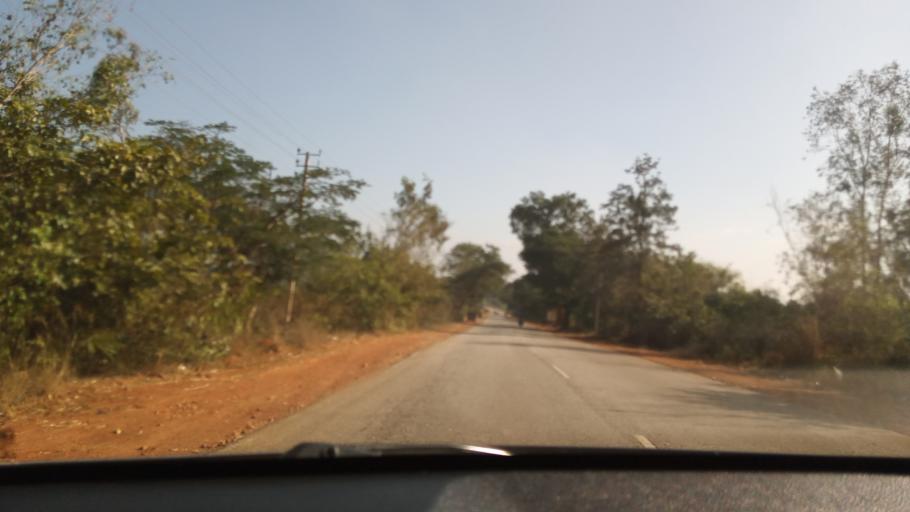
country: IN
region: Karnataka
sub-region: Bangalore Rural
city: Vijayapura
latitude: 13.2760
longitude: 77.7562
